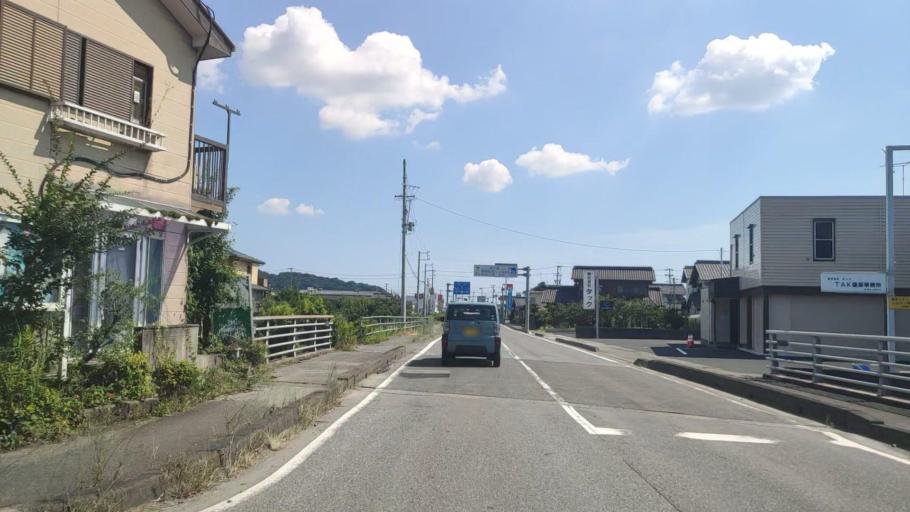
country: JP
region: Gifu
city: Godo
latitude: 35.4877
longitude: 136.6735
